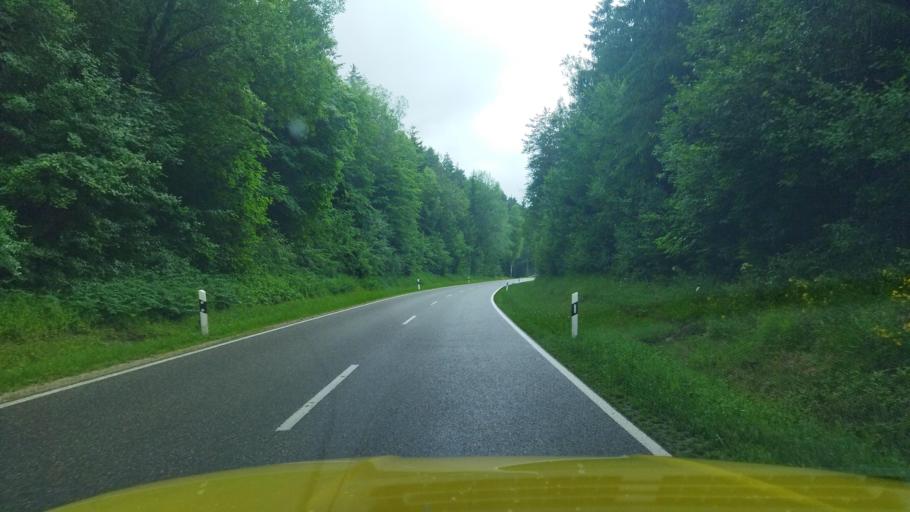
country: DE
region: Bavaria
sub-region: Lower Bavaria
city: Riedenburg
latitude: 48.9487
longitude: 11.6046
